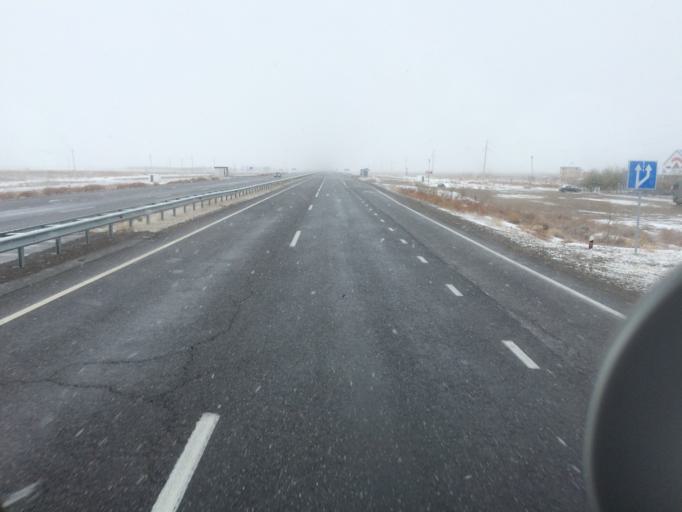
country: KZ
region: Ongtustik Qazaqstan
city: Turkestan
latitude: 43.4569
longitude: 67.9342
